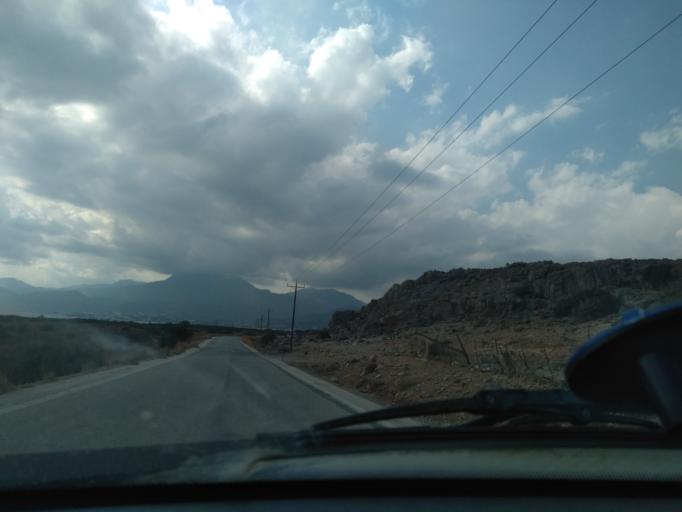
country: GR
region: Crete
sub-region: Nomos Lasithiou
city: Makry-Gialos
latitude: 35.0227
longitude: 26.0159
